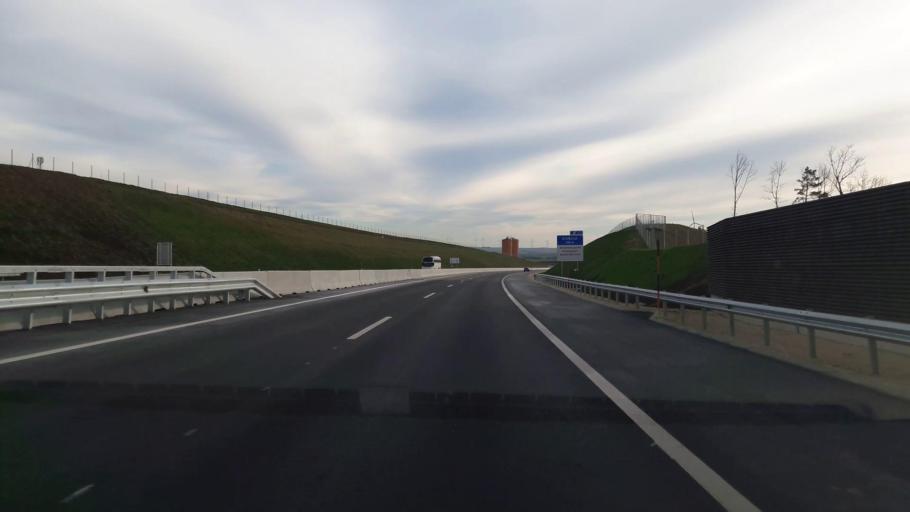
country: AT
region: Lower Austria
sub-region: Politischer Bezirk Mistelbach
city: Herrnbaumgarten
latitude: 48.6595
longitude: 16.6884
